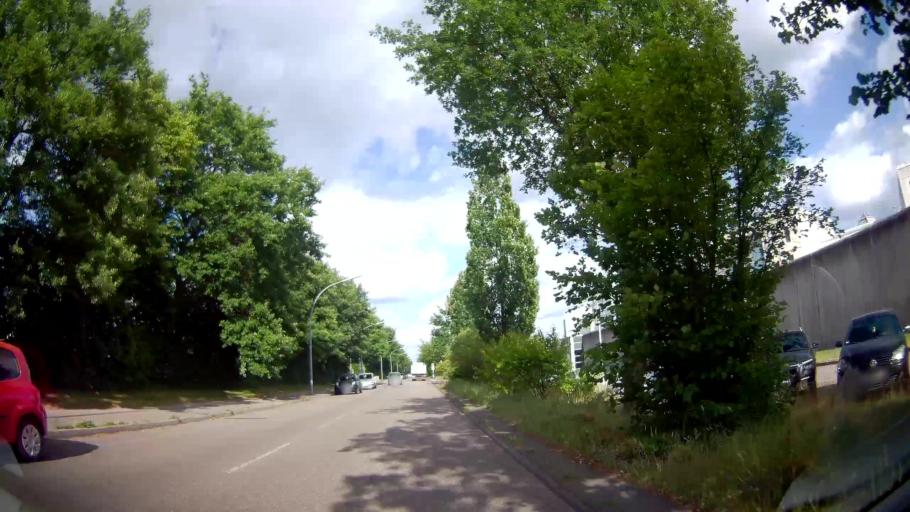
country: DE
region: North Rhine-Westphalia
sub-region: Regierungsbezirk Munster
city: Gelsenkirchen
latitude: 51.5139
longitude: 7.0556
